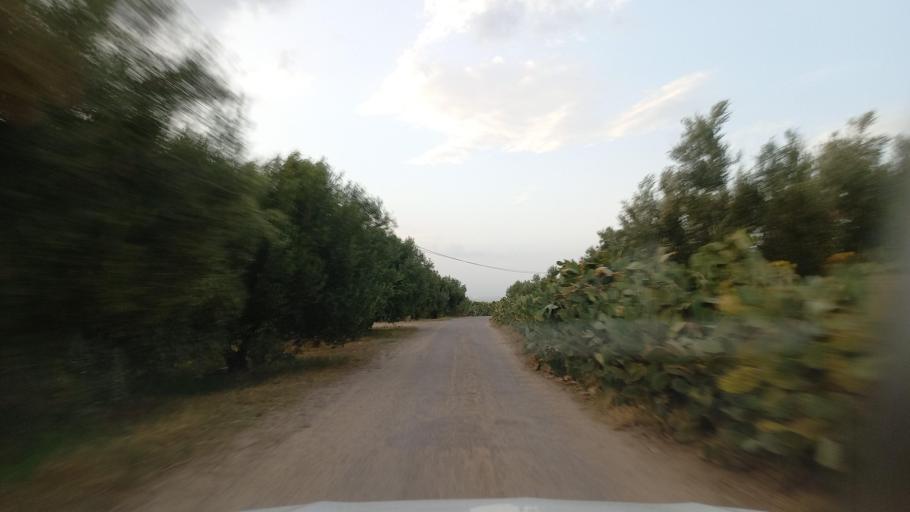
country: TN
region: Al Qasrayn
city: Kasserine
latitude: 35.2792
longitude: 9.0507
